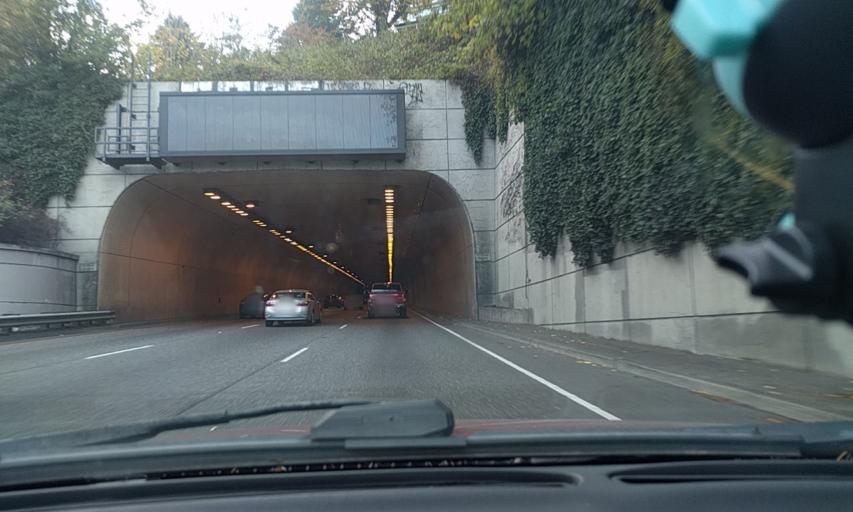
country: US
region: Oregon
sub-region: Multnomah County
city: Portland
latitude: 45.5157
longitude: -122.6944
